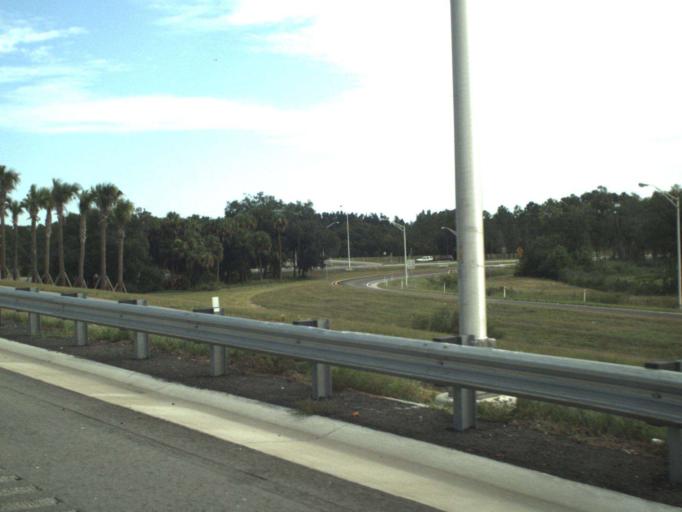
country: US
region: Florida
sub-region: Saint Lucie County
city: Lakewood Park
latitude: 27.4455
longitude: -80.3929
